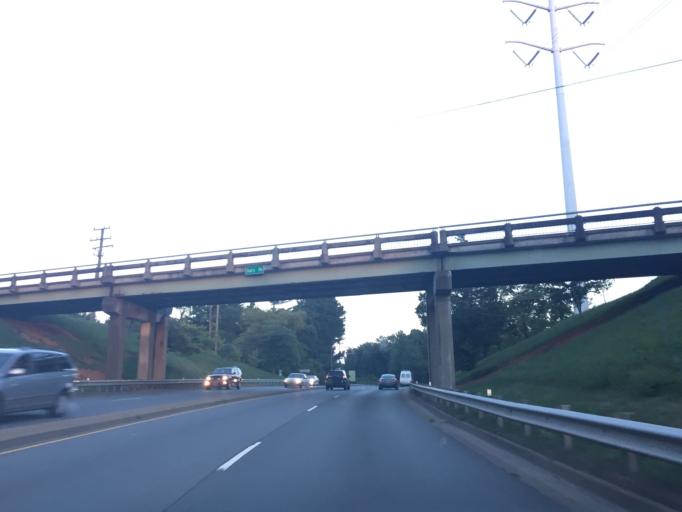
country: US
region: Virginia
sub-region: City of Charlottesville
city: Charlottesville
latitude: 38.0559
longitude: -78.4847
